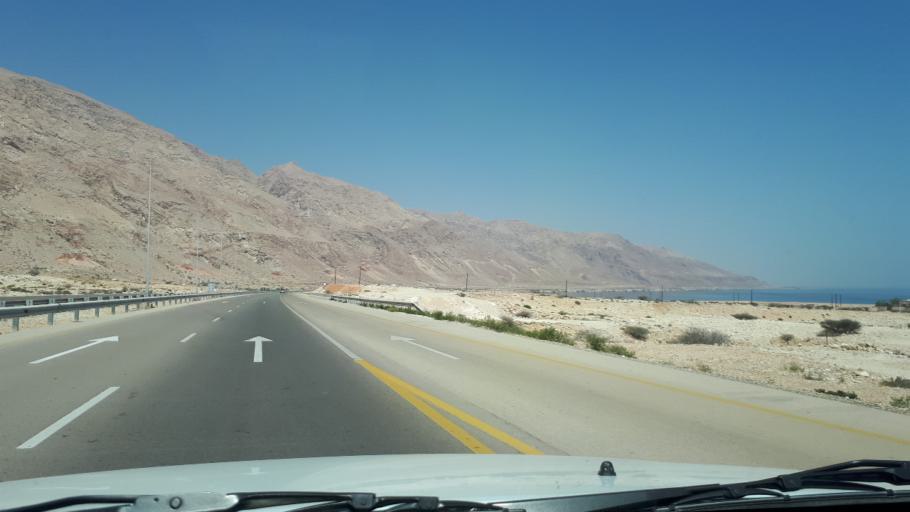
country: OM
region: Ash Sharqiyah
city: Sur
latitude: 22.7473
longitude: 59.3187
